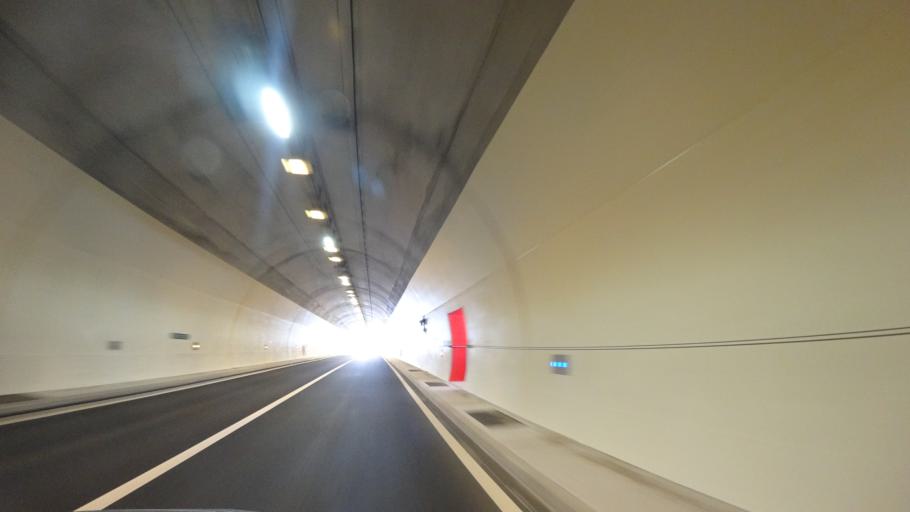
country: FR
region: Corsica
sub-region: Departement de la Corse-du-Sud
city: Propriano
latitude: 41.6729
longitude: 8.9276
